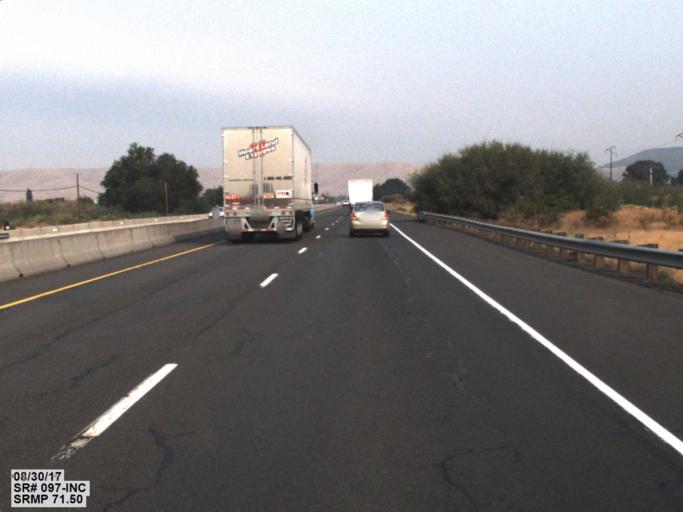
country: US
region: Washington
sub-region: Yakima County
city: Wapato
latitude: 46.4798
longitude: -120.4485
